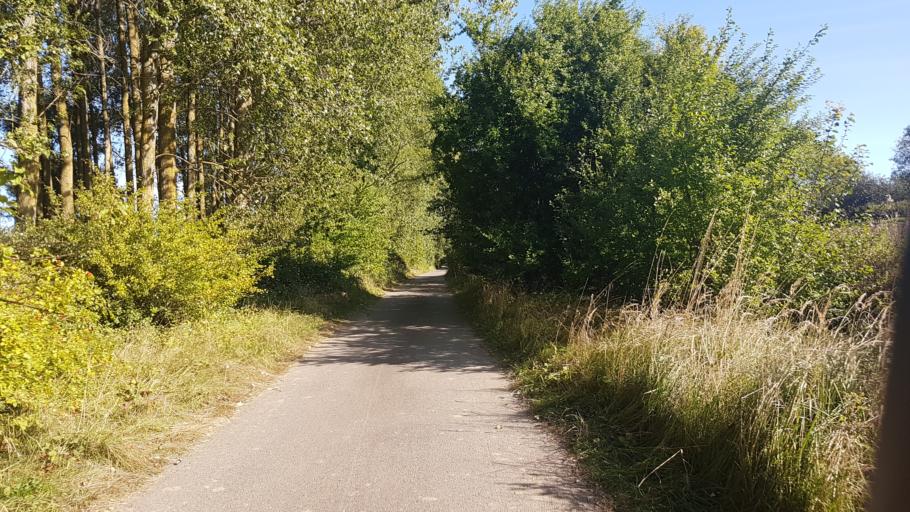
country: DE
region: Mecklenburg-Vorpommern
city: Sagard
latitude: 54.5093
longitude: 13.5245
